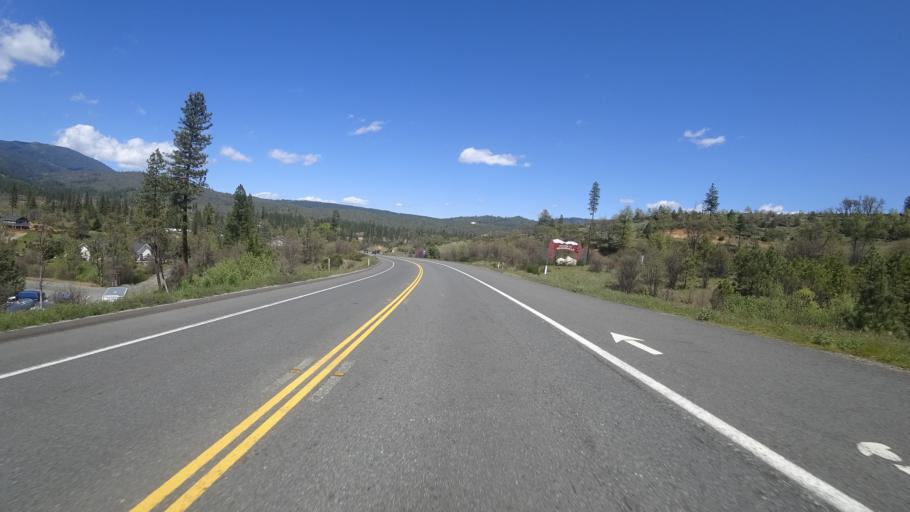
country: US
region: California
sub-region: Trinity County
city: Weaverville
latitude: 40.7348
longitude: -122.9546
